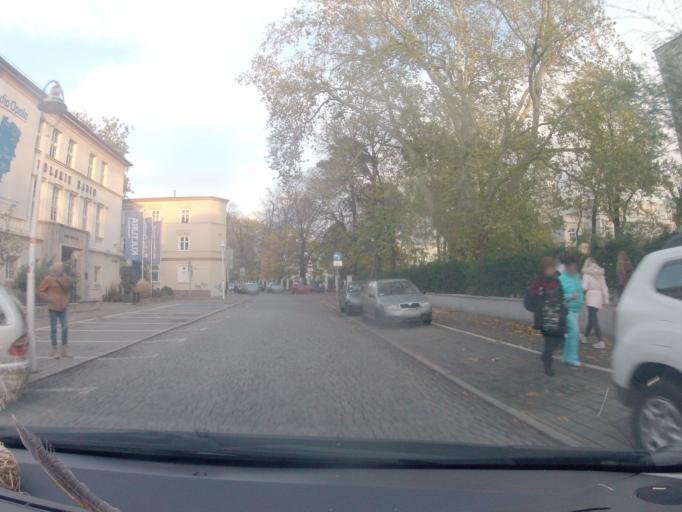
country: PL
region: Opole Voivodeship
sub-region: Powiat opolski
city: Opole
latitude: 50.6653
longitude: 17.9198
